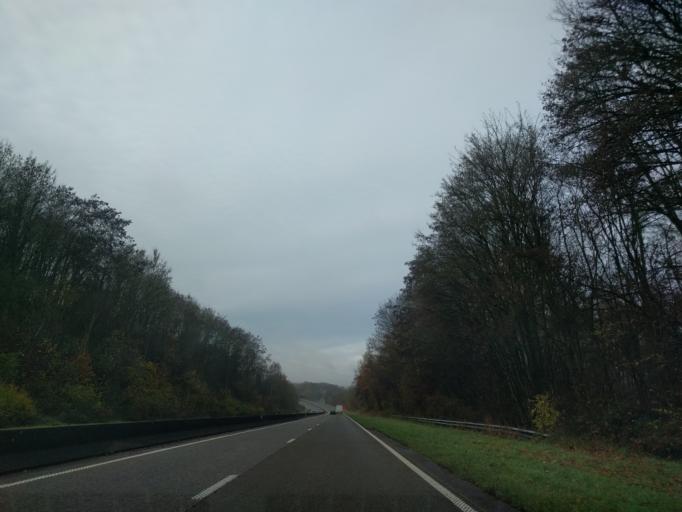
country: BE
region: Wallonia
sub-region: Province de Namur
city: Onhaye
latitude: 50.2438
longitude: 4.8566
